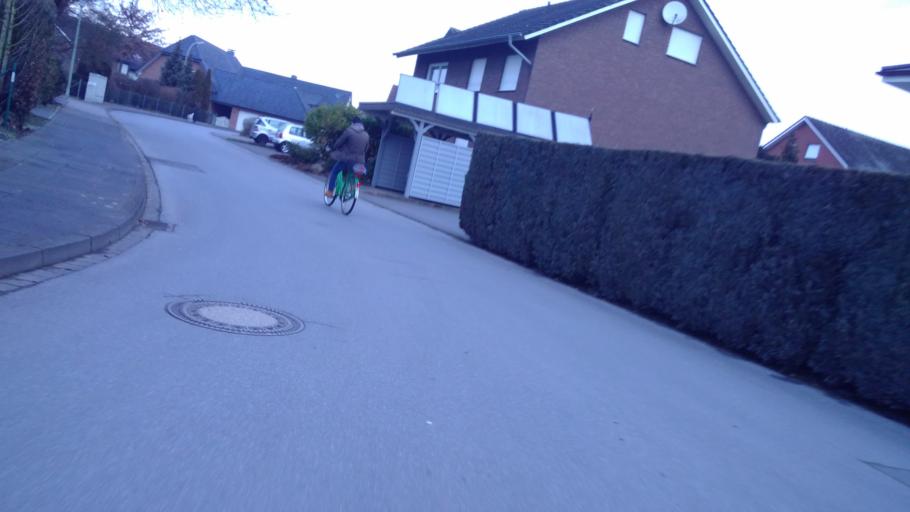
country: DE
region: North Rhine-Westphalia
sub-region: Regierungsbezirk Detmold
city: Verl
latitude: 51.8708
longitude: 8.5038
